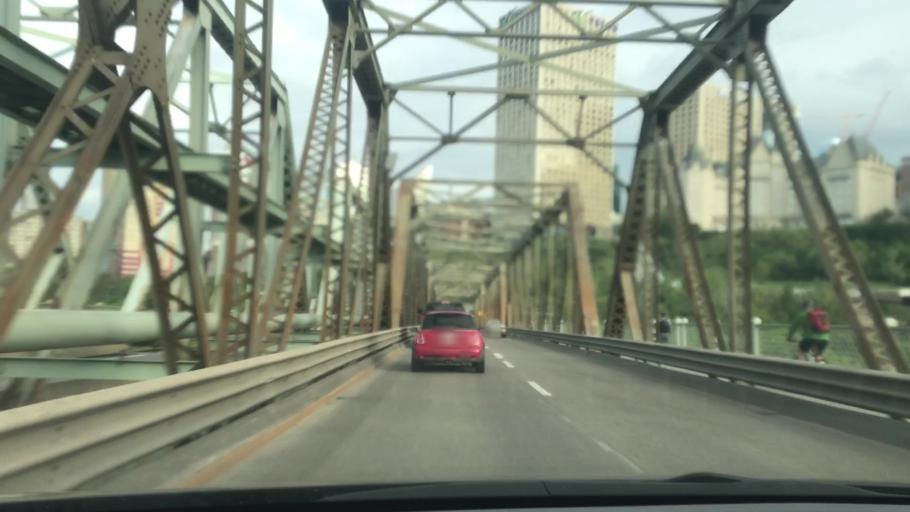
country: CA
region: Alberta
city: Edmonton
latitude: 53.5376
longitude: -113.4855
